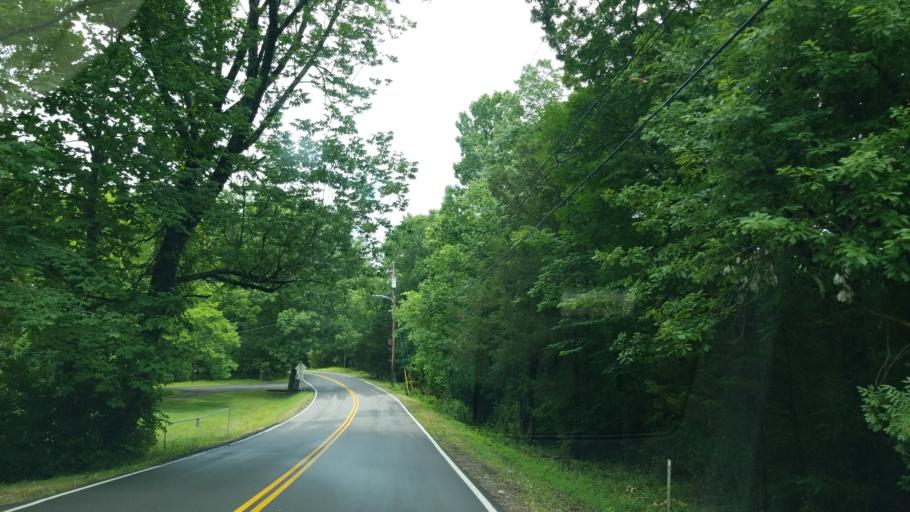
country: US
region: Tennessee
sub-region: Rutherford County
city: La Vergne
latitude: 36.1002
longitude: -86.6348
